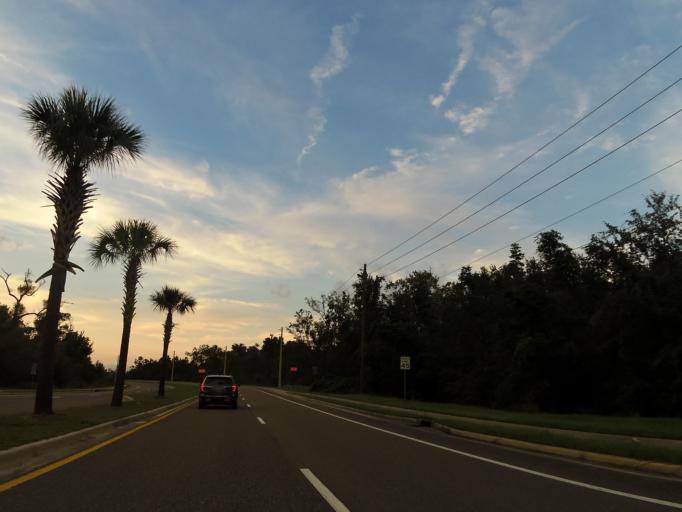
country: US
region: Florida
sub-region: Saint Johns County
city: Fruit Cove
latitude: 30.0854
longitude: -81.5322
